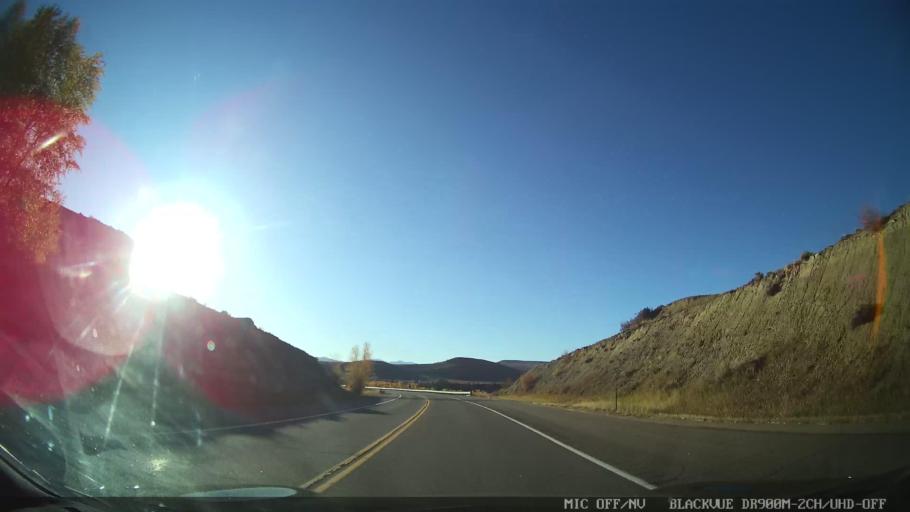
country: US
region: Colorado
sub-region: Grand County
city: Hot Sulphur Springs
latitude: 40.0537
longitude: -106.1738
